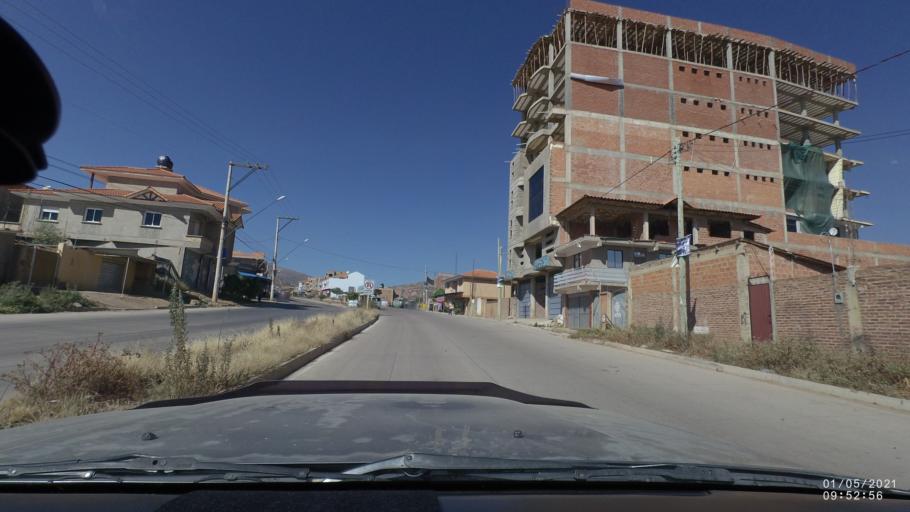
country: BO
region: Cochabamba
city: Cochabamba
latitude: -17.4816
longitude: -66.1732
